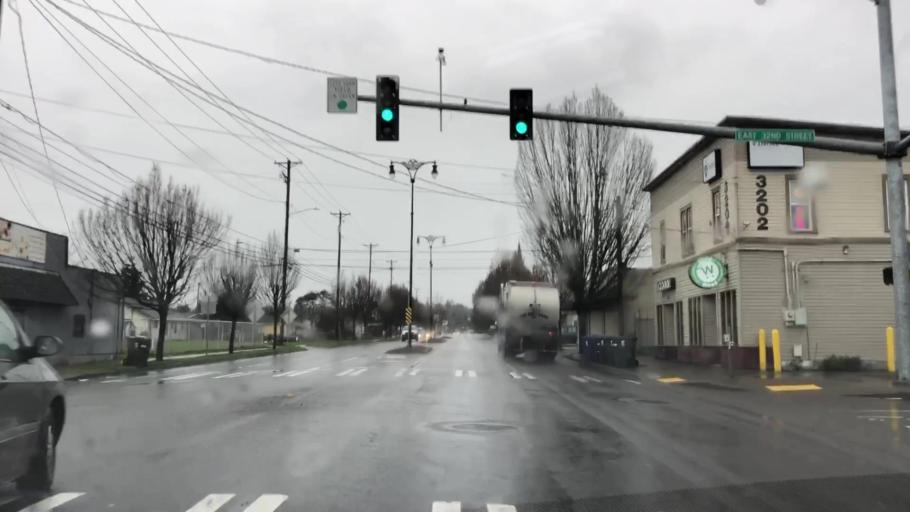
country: US
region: Washington
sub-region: Pierce County
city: Tacoma
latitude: 47.2348
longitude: -122.4096
